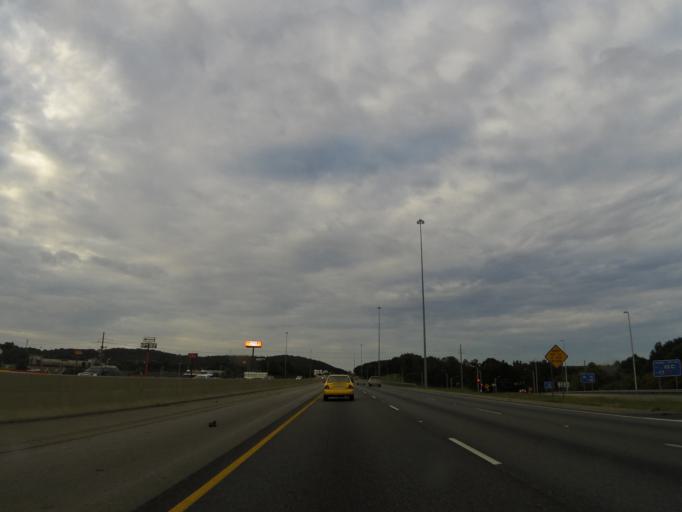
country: US
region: Alabama
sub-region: Shelby County
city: Indian Springs Village
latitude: 33.3350
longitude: -86.7795
